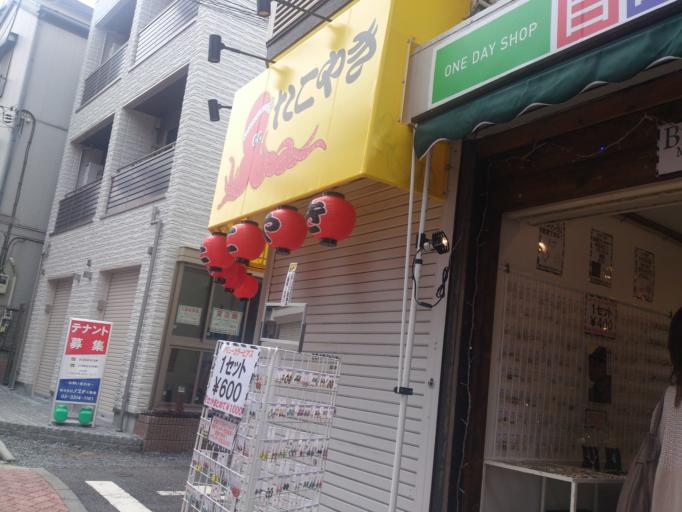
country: JP
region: Tokyo
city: Tokyo
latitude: 35.7024
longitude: 139.6479
